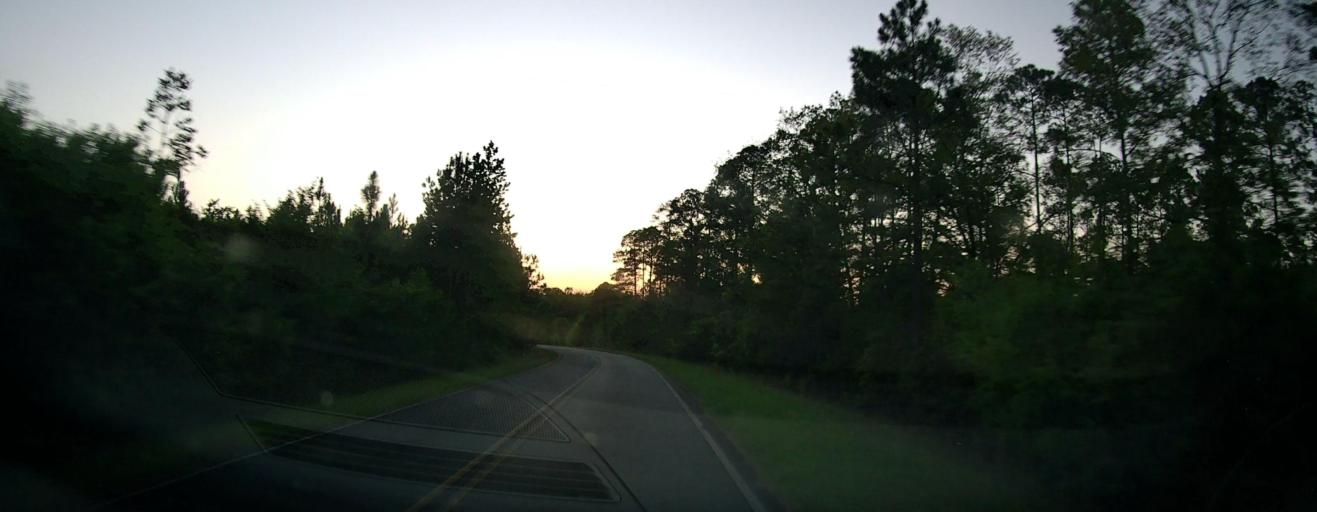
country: US
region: Georgia
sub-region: Marion County
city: Buena Vista
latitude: 32.2551
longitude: -84.6209
